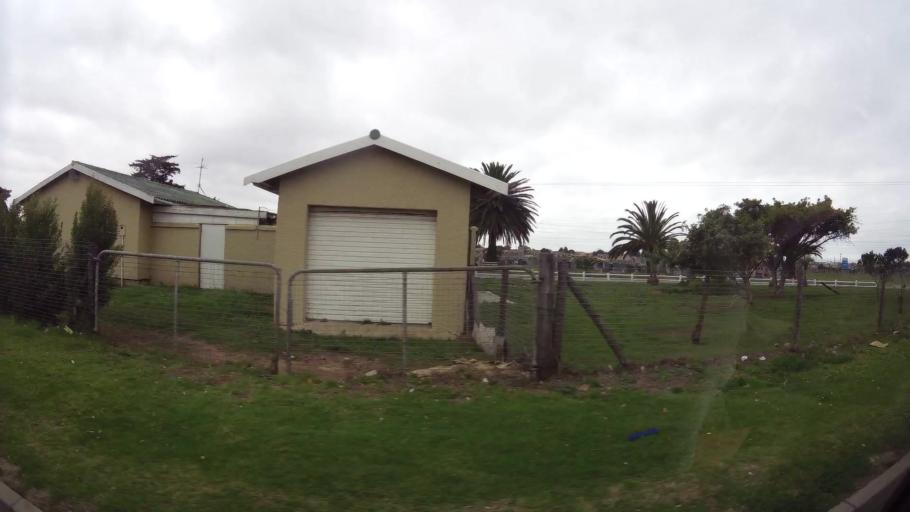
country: ZA
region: Eastern Cape
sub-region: Nelson Mandela Bay Metropolitan Municipality
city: Port Elizabeth
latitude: -33.9190
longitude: 25.5648
